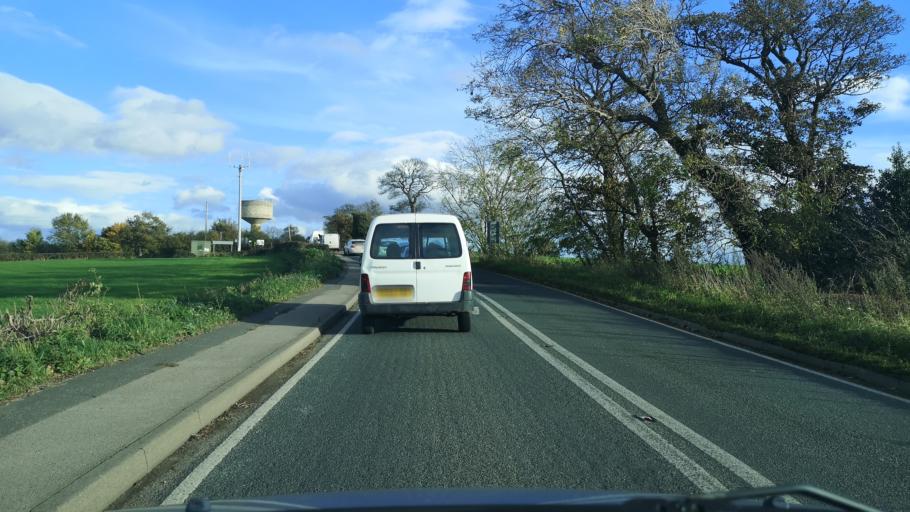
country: GB
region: England
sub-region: City and Borough of Wakefield
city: Middlestown
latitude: 53.6303
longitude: -1.6105
